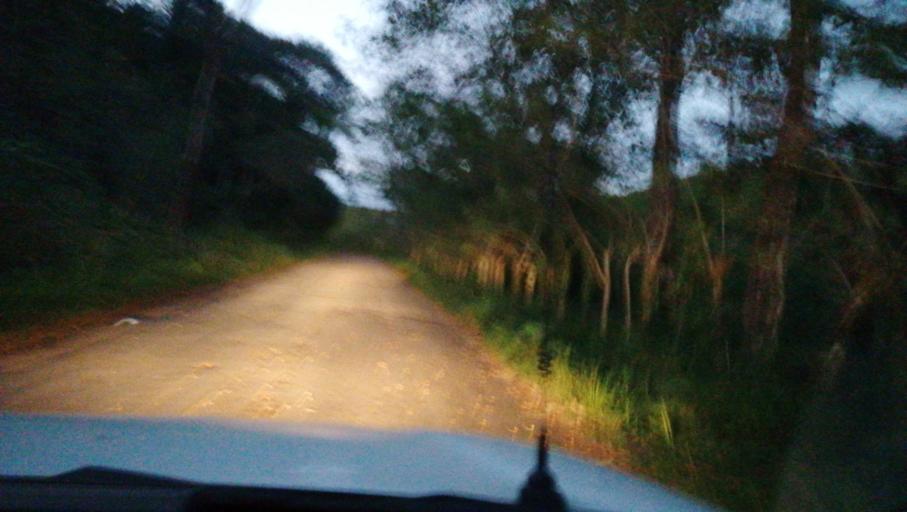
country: MX
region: Chiapas
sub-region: Ostuacan
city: Nuevo Juan del Grijalva
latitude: 17.4765
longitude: -93.3457
